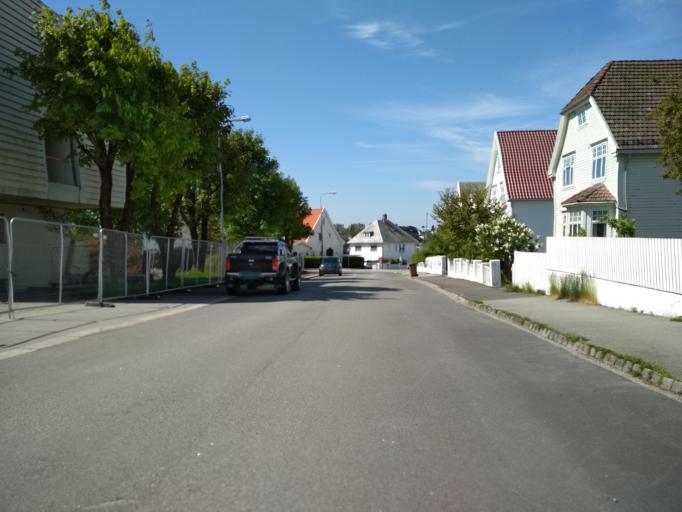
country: NO
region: Rogaland
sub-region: Stavanger
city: Stavanger
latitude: 58.9597
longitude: 5.7265
